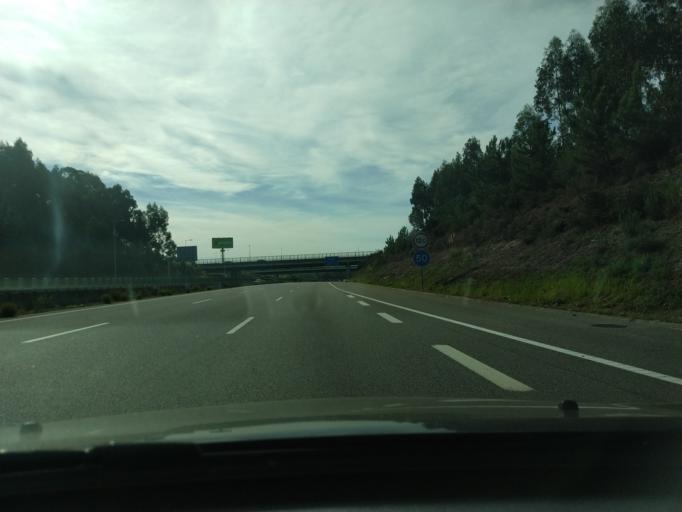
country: PT
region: Aveiro
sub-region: Santa Maria da Feira
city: Feira
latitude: 40.9265
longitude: -8.5685
